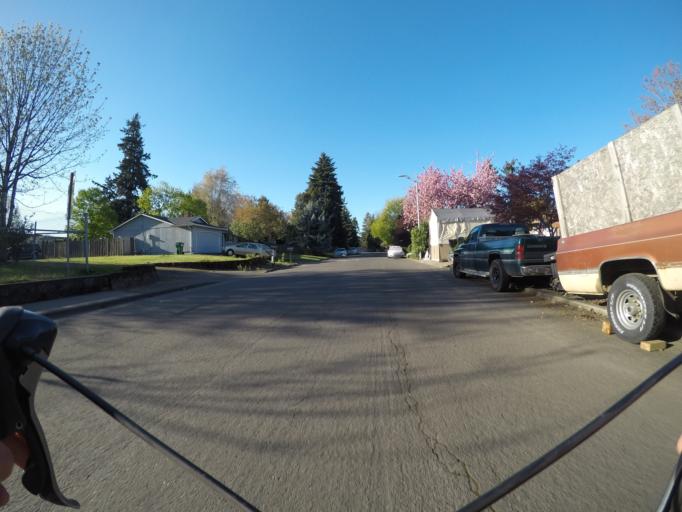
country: US
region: Oregon
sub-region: Washington County
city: Aloha
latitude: 45.4912
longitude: -122.8754
